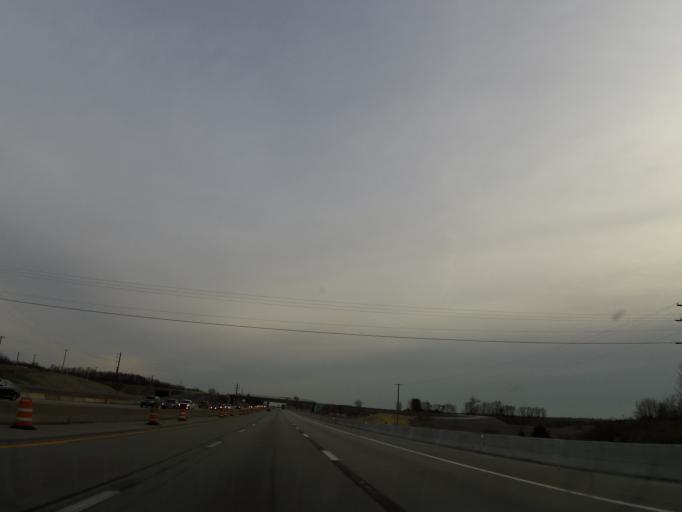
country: US
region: Kentucky
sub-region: Scott County
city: Georgetown
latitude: 38.2465
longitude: -84.5465
